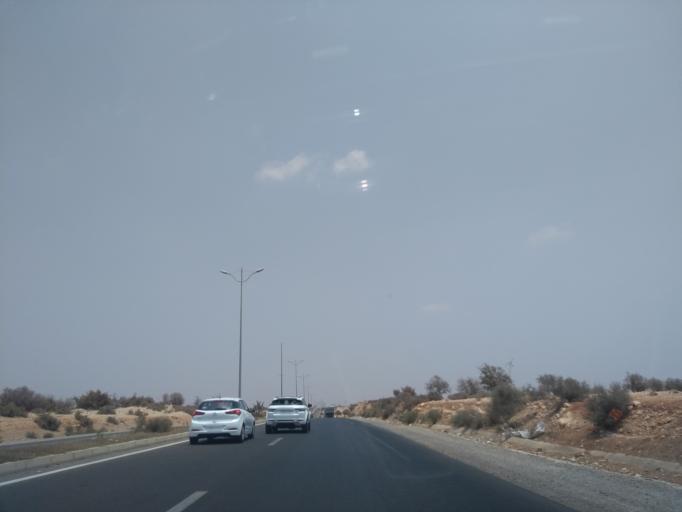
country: MA
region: Souss-Massa-Draa
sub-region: Inezgane-Ait Mellou
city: Inezgane
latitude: 30.4001
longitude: -9.4446
